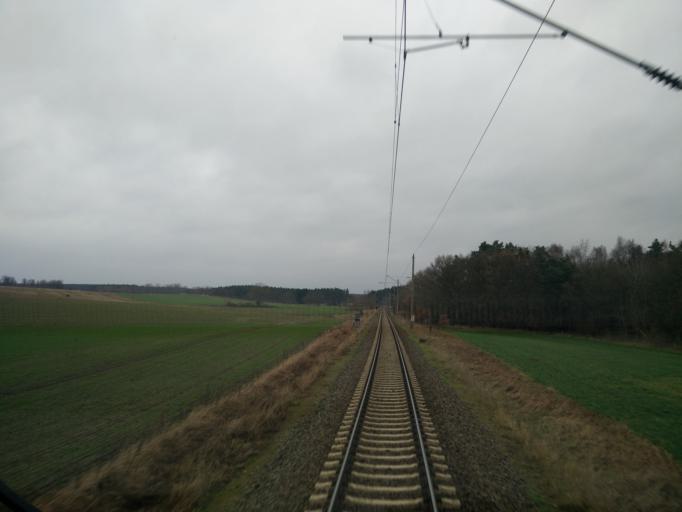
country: DE
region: Mecklenburg-Vorpommern
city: Bad Kleinen
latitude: 53.7808
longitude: 11.4868
